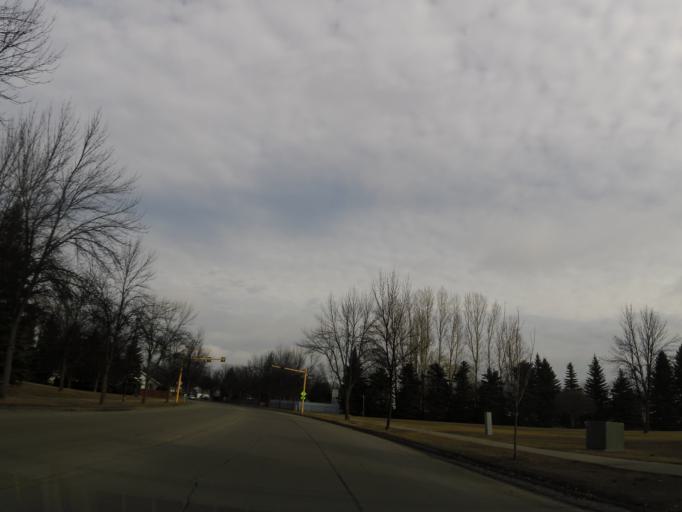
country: US
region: North Dakota
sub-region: Grand Forks County
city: Grand Forks
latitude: 47.9085
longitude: -97.0625
